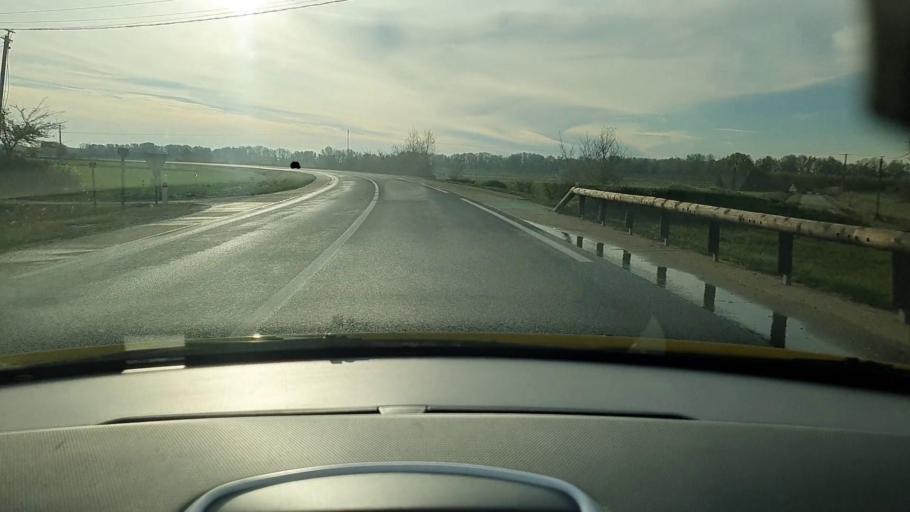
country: FR
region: Languedoc-Roussillon
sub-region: Departement du Gard
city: Bellegarde
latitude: 43.7104
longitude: 4.5494
